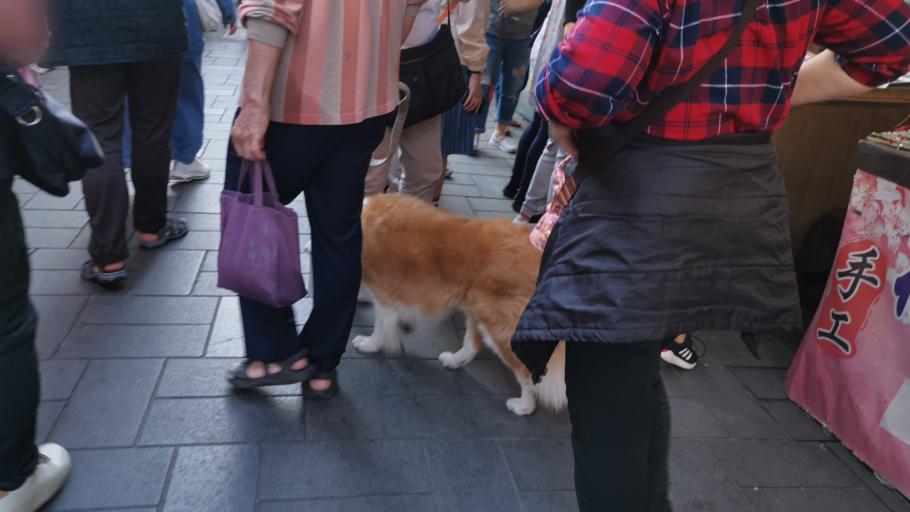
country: TW
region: Taiwan
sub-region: Keelung
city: Keelung
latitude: 25.2215
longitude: 121.6389
